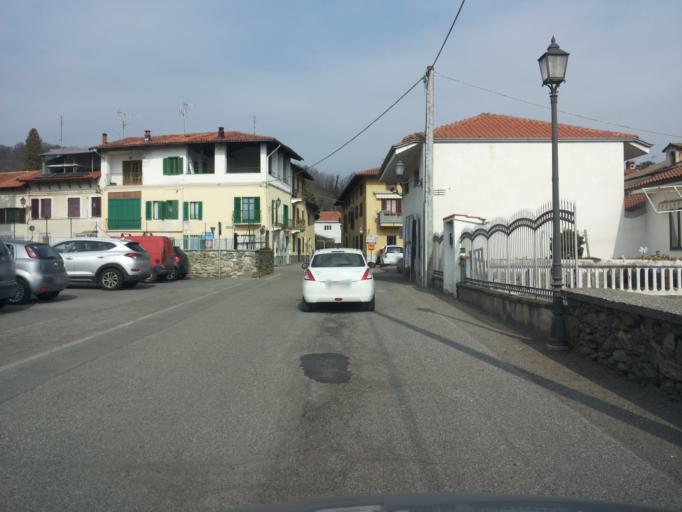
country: IT
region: Piedmont
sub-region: Provincia di Biella
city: Dorzano
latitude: 45.4248
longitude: 8.0966
